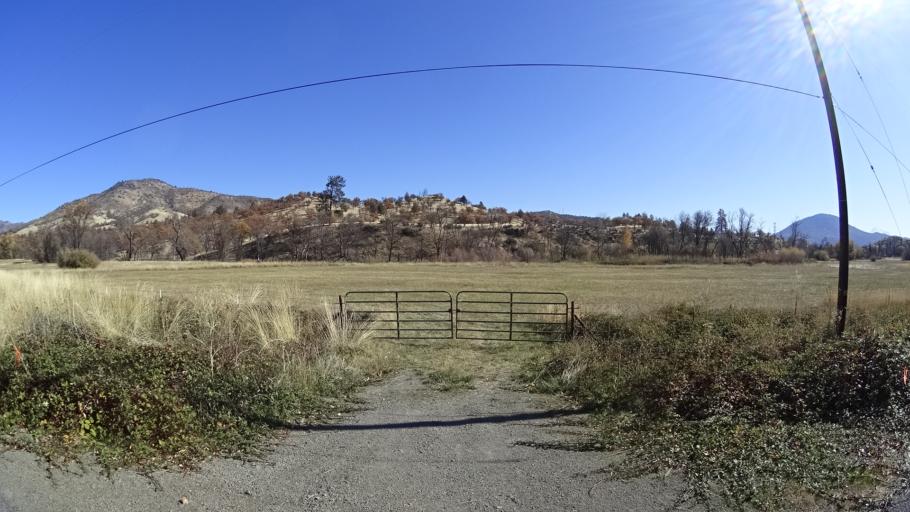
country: US
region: California
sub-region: Siskiyou County
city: Yreka
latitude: 41.9379
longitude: -122.5917
